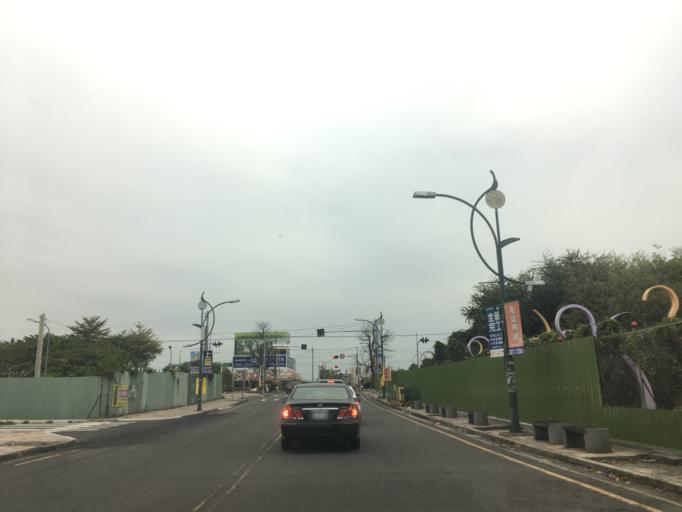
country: TW
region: Taiwan
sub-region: Nantou
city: Nantou
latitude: 23.8966
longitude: 120.5326
